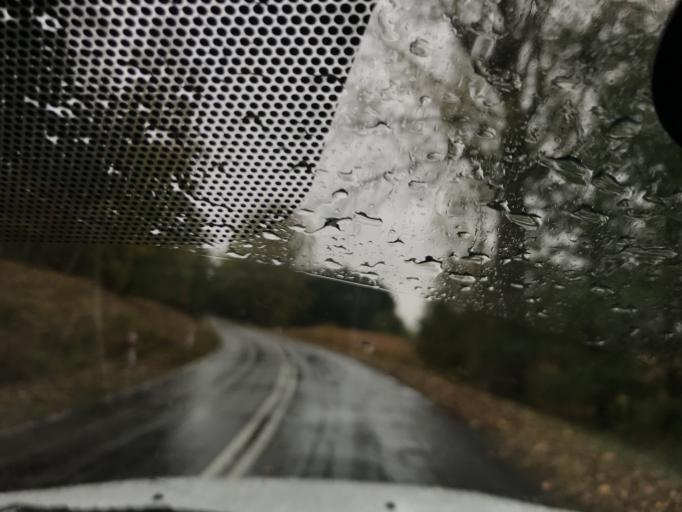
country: DE
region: Brandenburg
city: Neulewin
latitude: 52.7815
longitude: 14.2909
